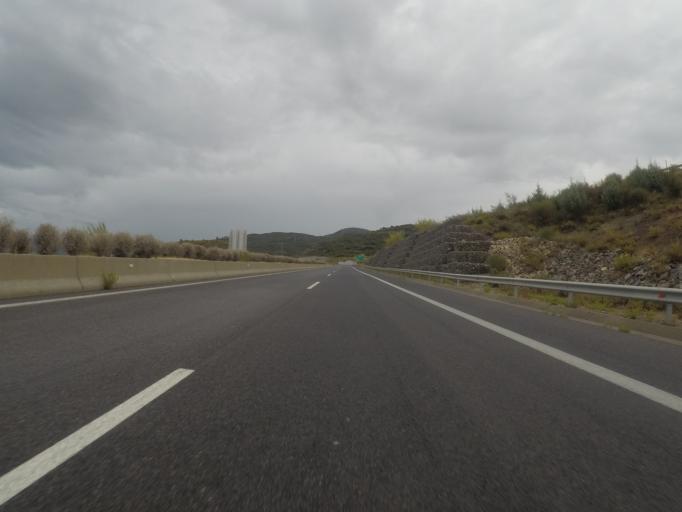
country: GR
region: Peloponnese
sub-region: Nomos Messinias
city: Meligalas
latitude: 37.2568
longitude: 22.0247
